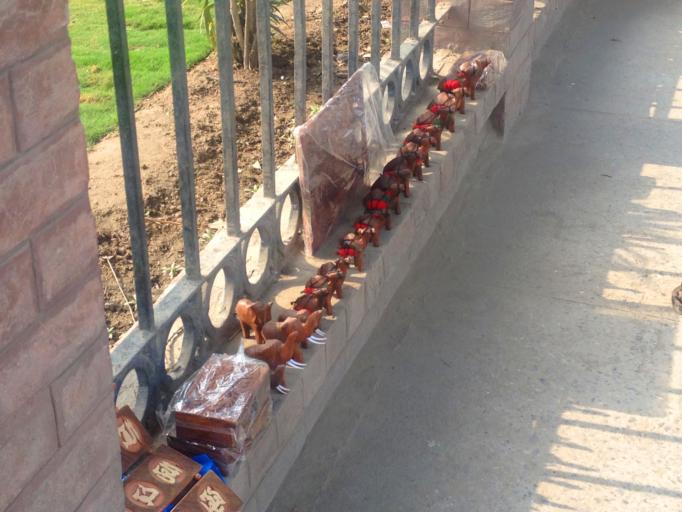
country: PK
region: Punjab
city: Lahore
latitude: 31.5688
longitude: 74.3087
